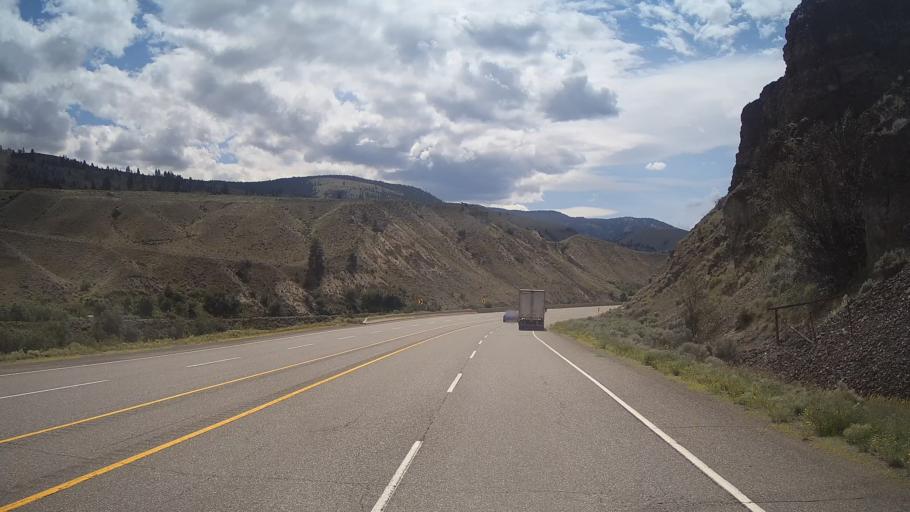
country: CA
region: British Columbia
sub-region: Thompson-Nicola Regional District
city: Ashcroft
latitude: 50.5140
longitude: -121.2829
